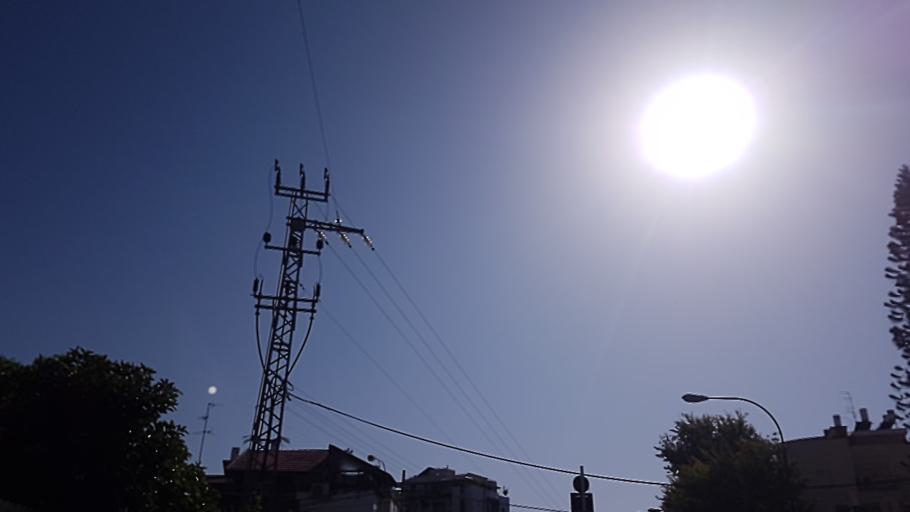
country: IL
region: Tel Aviv
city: Giv`atayim
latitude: 32.0627
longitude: 34.8230
